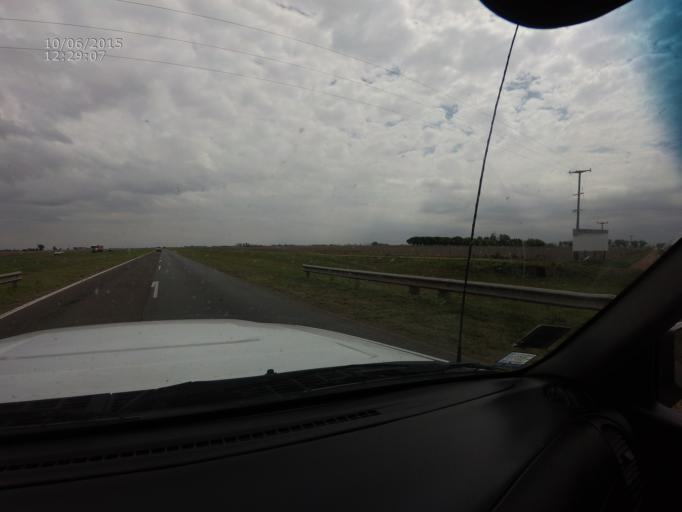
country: AR
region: Santa Fe
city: Carcarana
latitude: -32.8935
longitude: -61.0737
